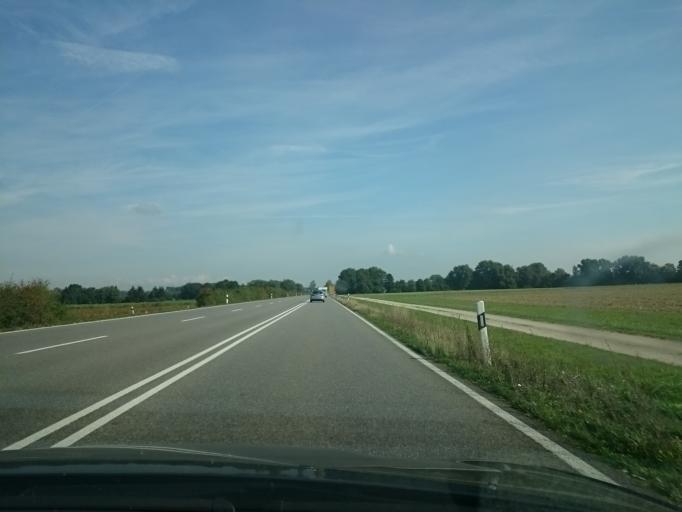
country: DE
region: Bavaria
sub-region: Upper Bavaria
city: Schrobenhausen
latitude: 48.5407
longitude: 11.2496
